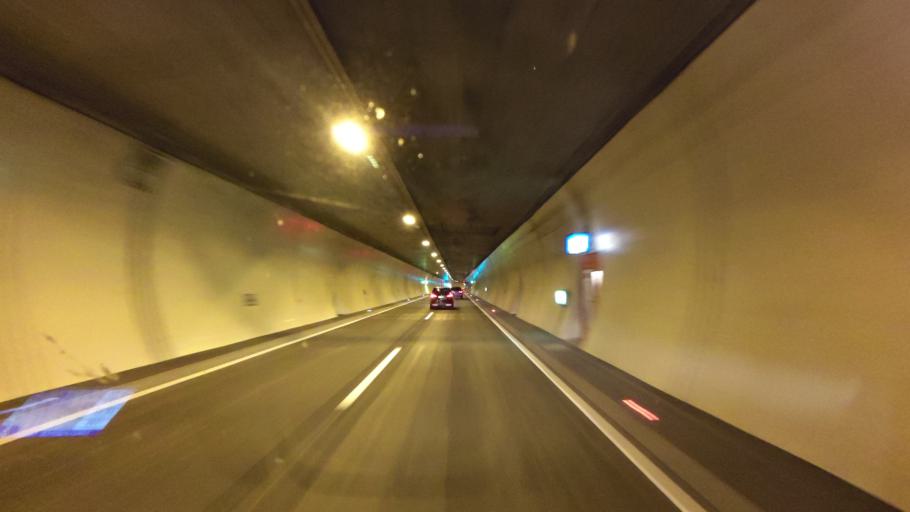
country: AT
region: Salzburg
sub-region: Politischer Bezirk Tamsweg
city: Sankt Michael im Lungau
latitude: 47.0326
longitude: 13.5984
